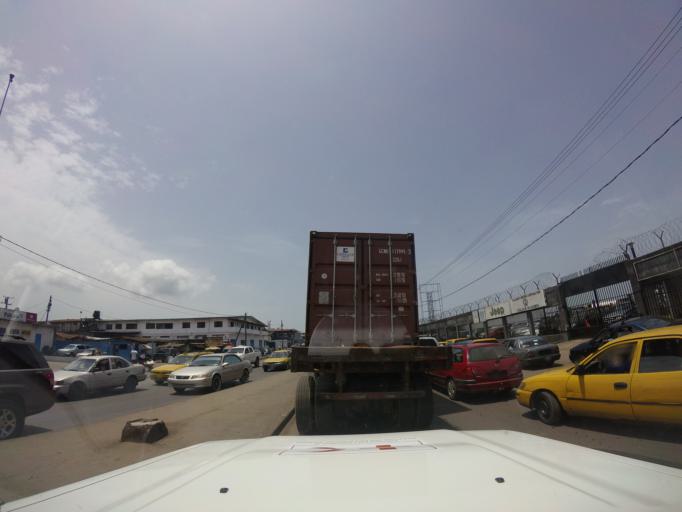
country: LR
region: Montserrado
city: Monrovia
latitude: 6.3320
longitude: -10.7987
